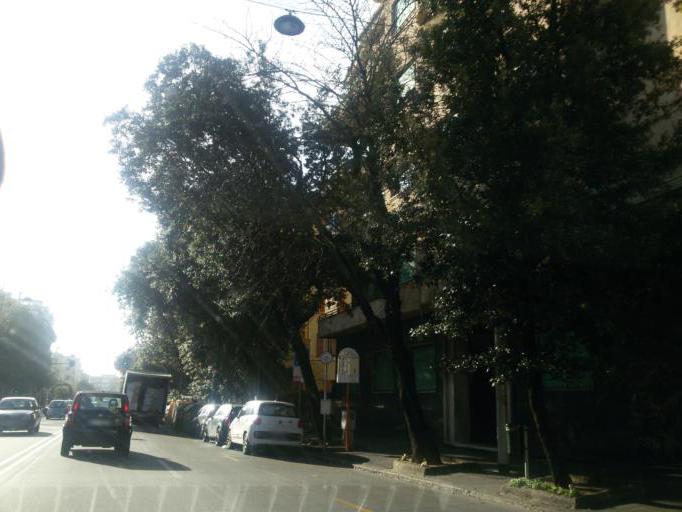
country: IT
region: Liguria
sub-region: Provincia di Genova
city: San Teodoro
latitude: 44.3930
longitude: 8.9705
